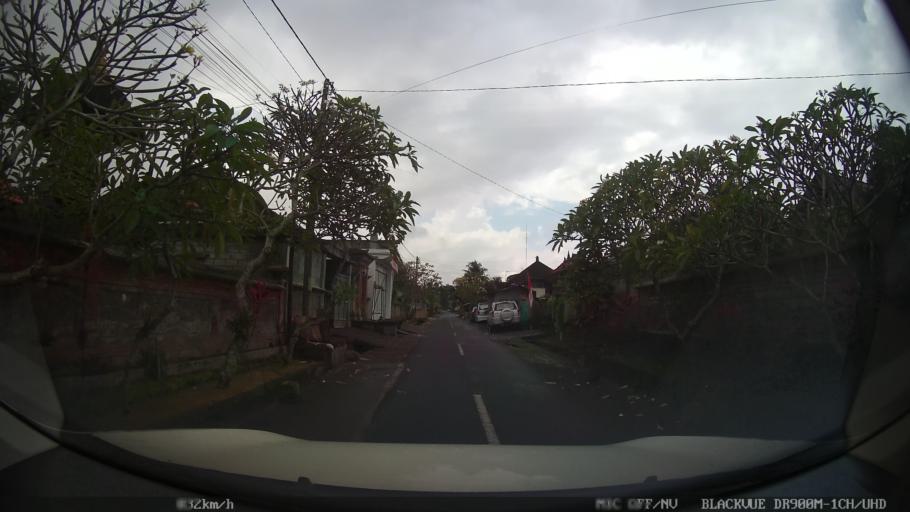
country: ID
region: Bali
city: Banjar Tebongkang
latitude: -8.5267
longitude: 115.2372
